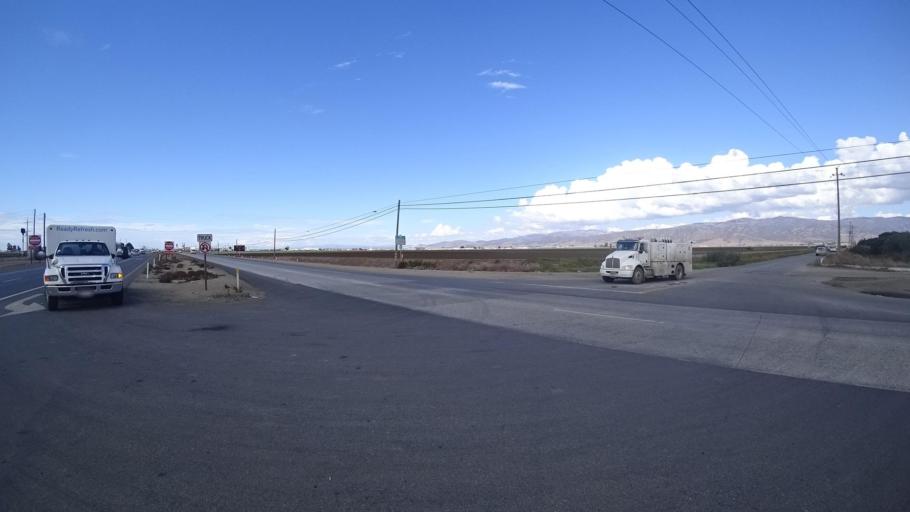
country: US
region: California
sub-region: Monterey County
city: Chualar
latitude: 36.6047
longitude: -121.5581
